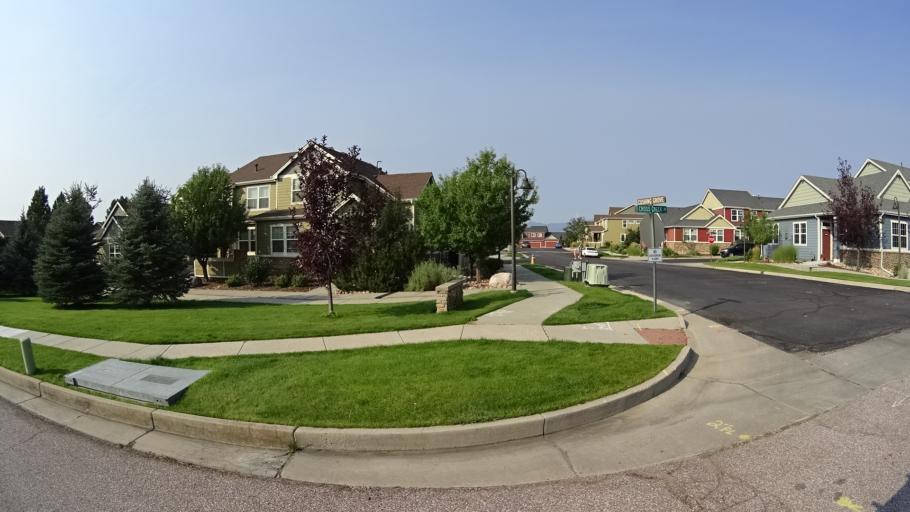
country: US
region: Colorado
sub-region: El Paso County
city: Black Forest
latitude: 38.9570
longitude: -104.7232
